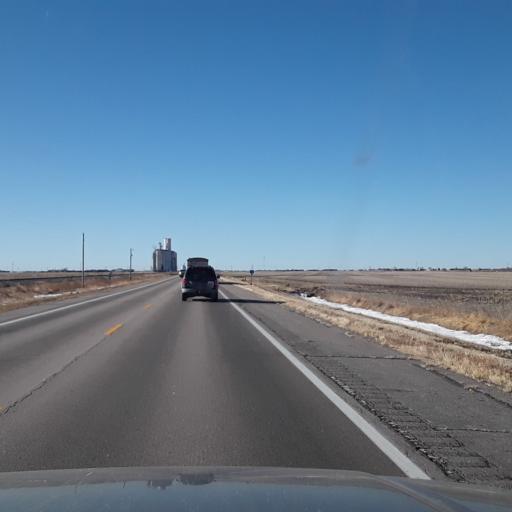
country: US
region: Nebraska
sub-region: Kearney County
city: Minden
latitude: 40.4940
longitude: -99.0135
